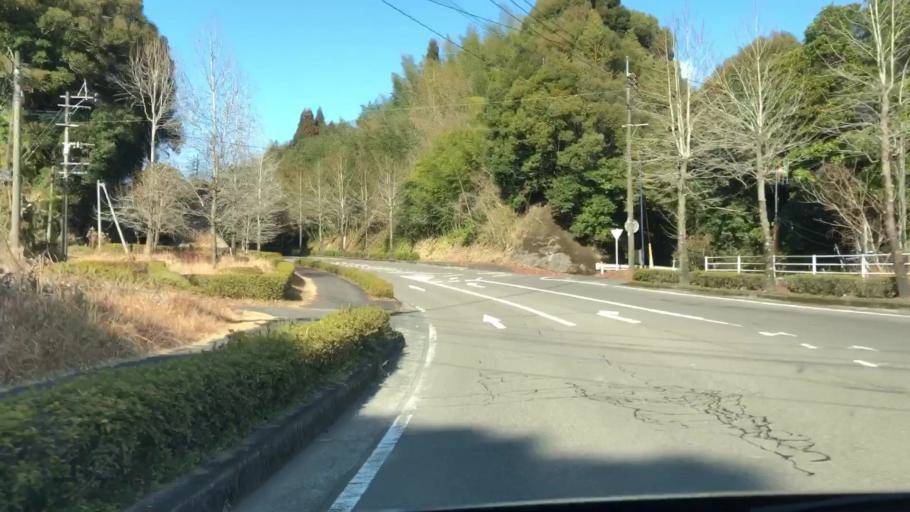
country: JP
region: Kagoshima
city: Satsumasendai
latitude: 31.8277
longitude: 130.4353
